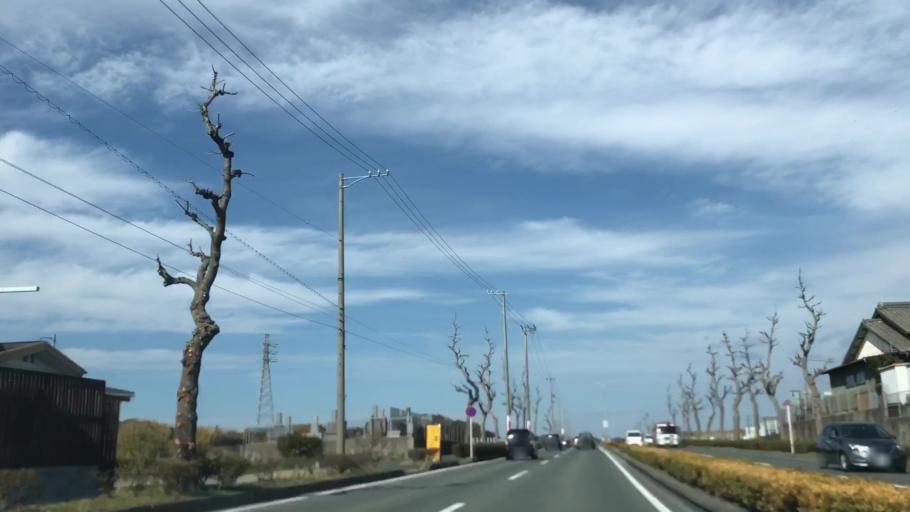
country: JP
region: Shizuoka
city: Hamamatsu
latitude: 34.7011
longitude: 137.6480
